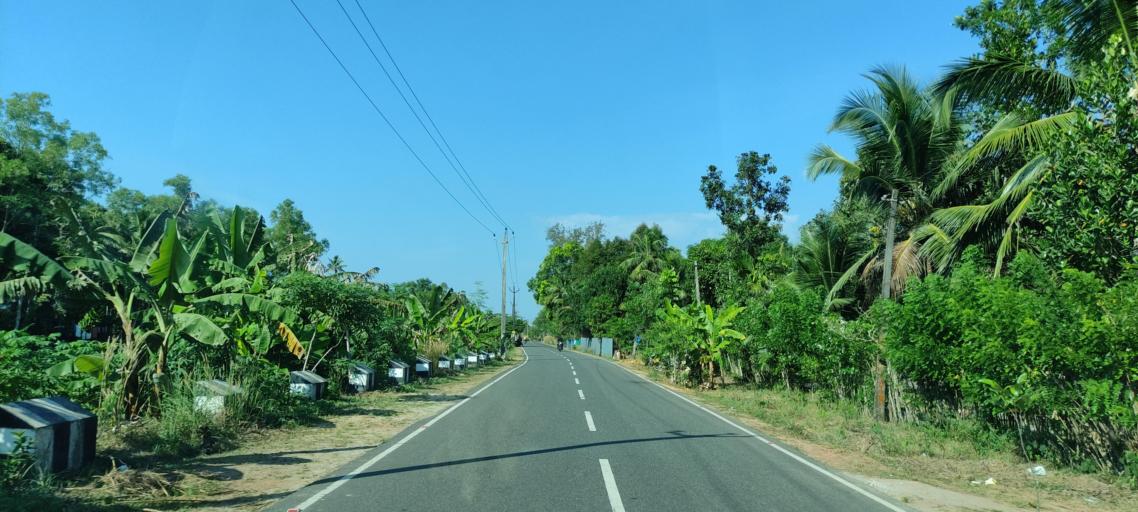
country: IN
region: Kerala
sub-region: Alappuzha
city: Alleppey
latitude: 9.5787
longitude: 76.3317
